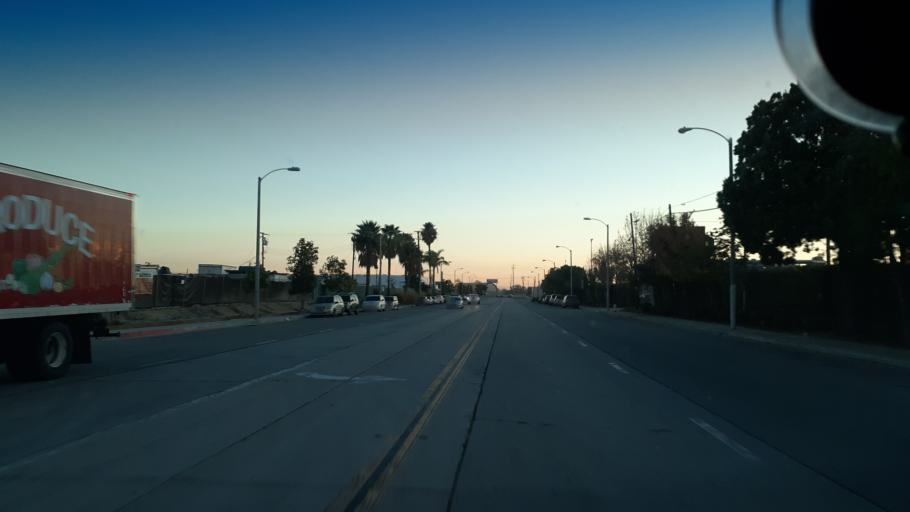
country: US
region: California
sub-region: Los Angeles County
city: Carson
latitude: 33.8597
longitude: -118.2785
